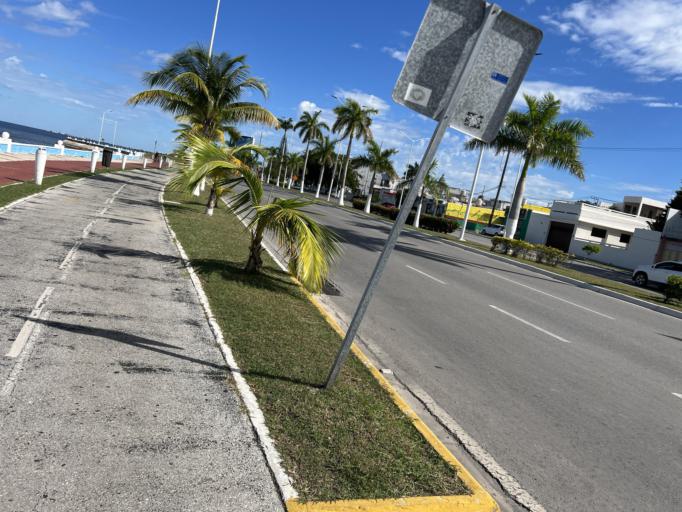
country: MX
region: Campeche
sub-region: Campeche
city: Campeche
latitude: 19.8407
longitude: -90.5472
